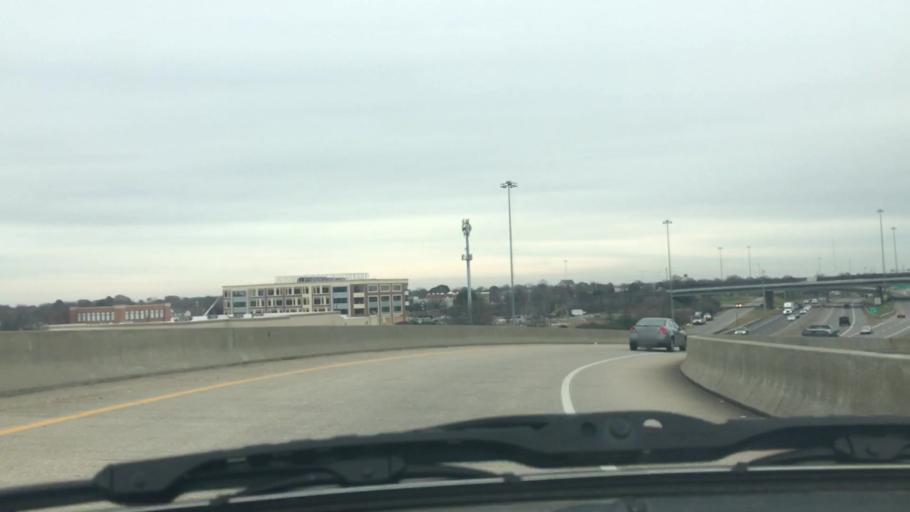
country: US
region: Virginia
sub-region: City of Newport News
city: Newport News
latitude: 36.9854
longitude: -76.4278
